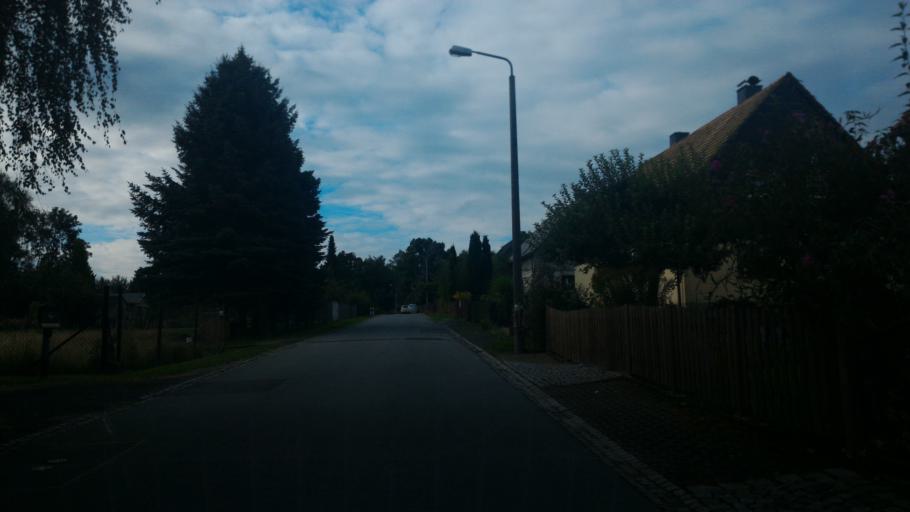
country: DE
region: Saxony
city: Neugersdorf
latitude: 50.9687
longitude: 14.6146
